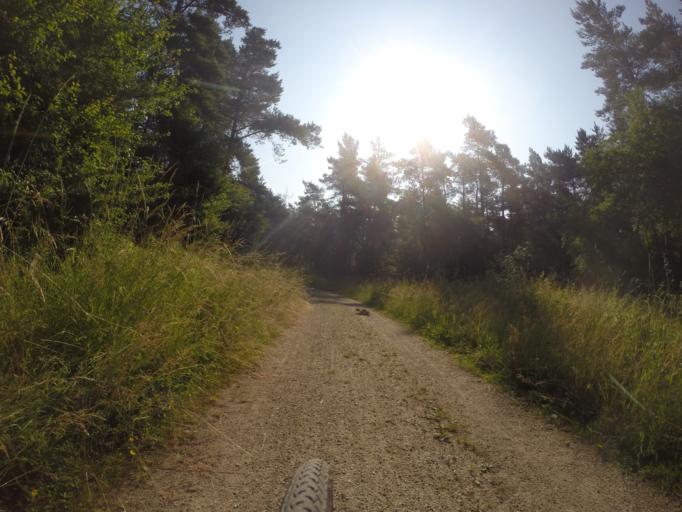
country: DK
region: Capital Region
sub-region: Ballerup Kommune
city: Ballerup
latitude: 55.7027
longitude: 12.3411
